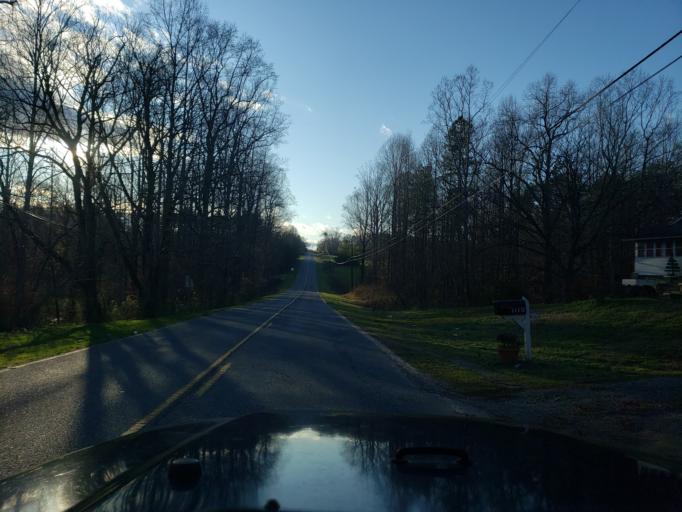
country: US
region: North Carolina
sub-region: Cleveland County
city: Shelby
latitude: 35.4153
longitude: -81.5769
